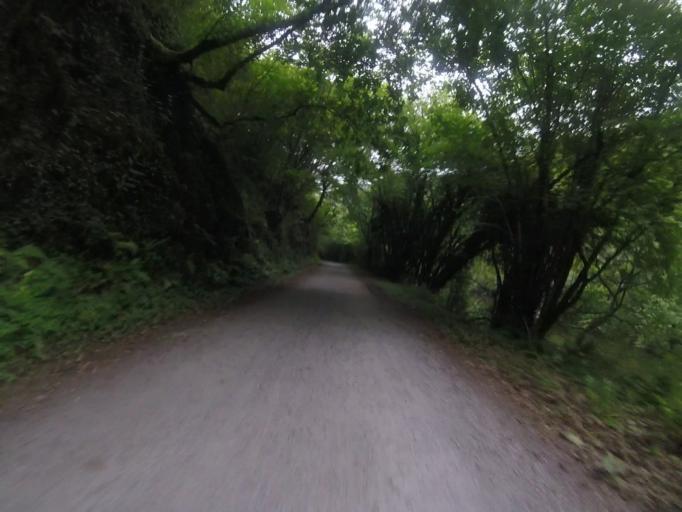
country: ES
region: Navarre
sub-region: Provincia de Navarra
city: Etxalar
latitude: 43.2075
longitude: -1.6628
